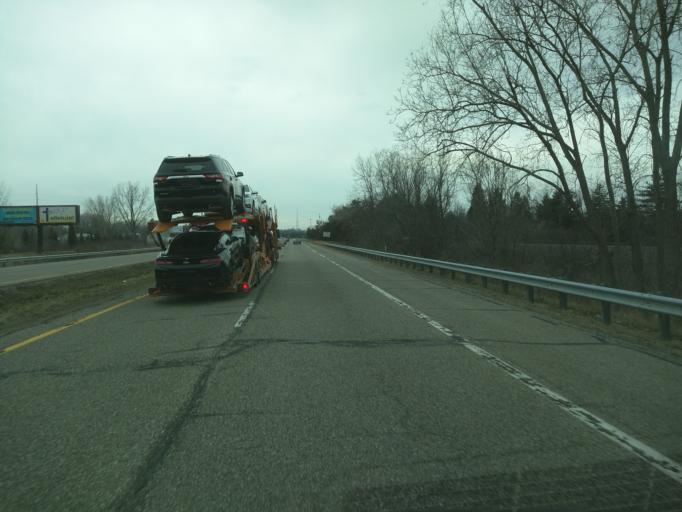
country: US
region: Michigan
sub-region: Eaton County
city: Waverly
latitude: 42.7152
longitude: -84.6052
